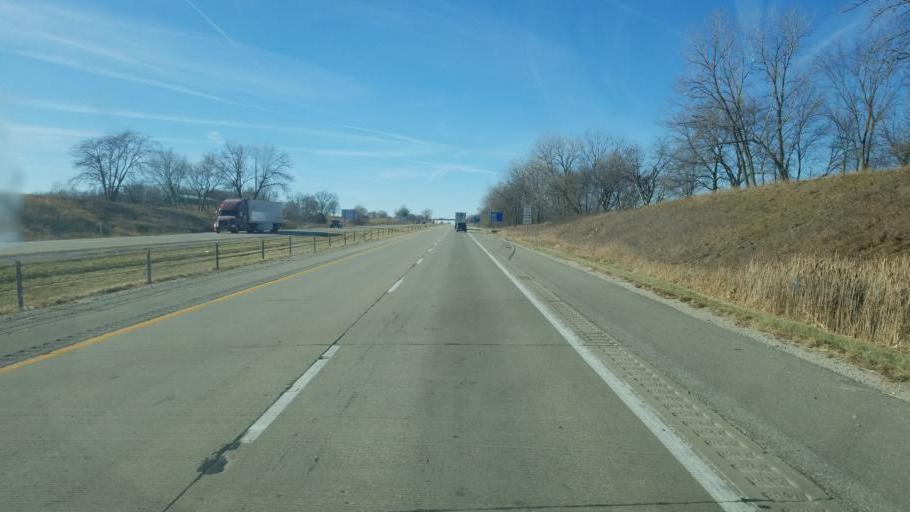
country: US
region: Iowa
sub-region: Dallas County
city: Waukee
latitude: 41.5651
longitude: -93.8661
